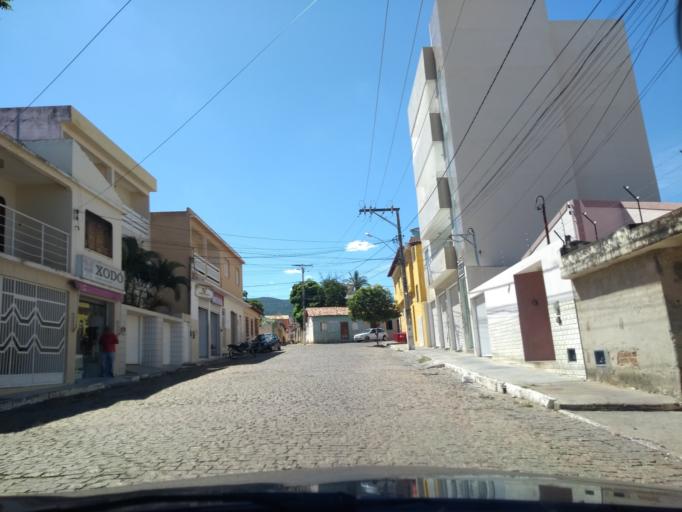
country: BR
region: Bahia
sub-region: Brumado
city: Brumado
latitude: -14.2060
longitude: -41.6687
